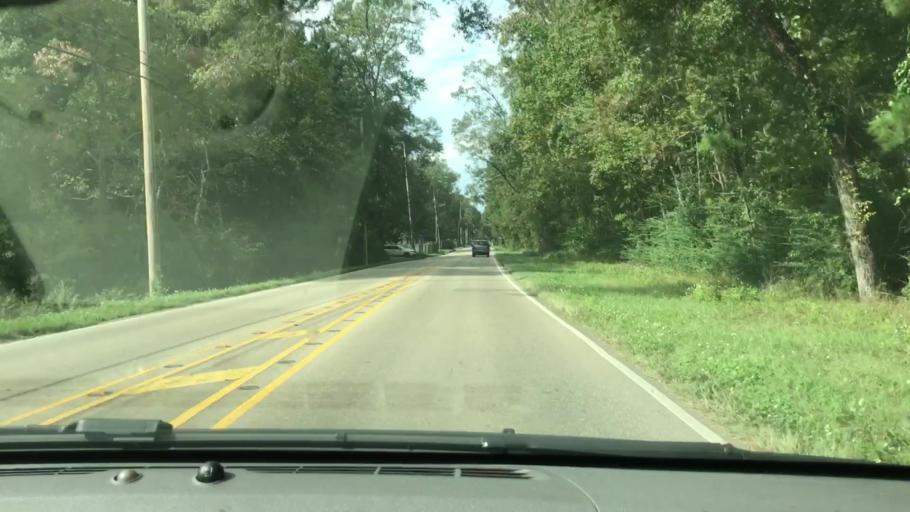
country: US
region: Louisiana
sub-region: Saint Tammany Parish
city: Abita Springs
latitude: 30.4600
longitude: -90.0612
